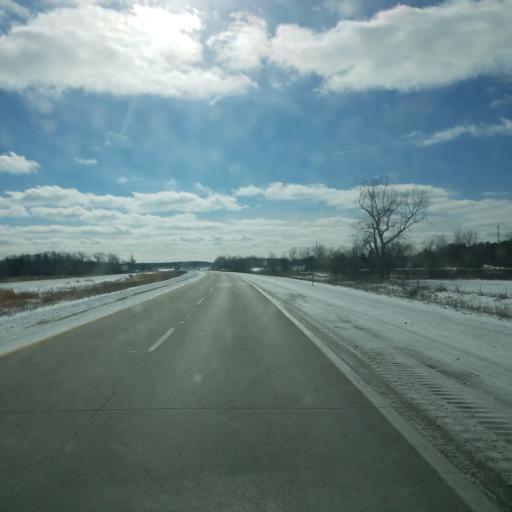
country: US
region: Michigan
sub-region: Clinton County
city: Saint Johns
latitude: 42.9192
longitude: -84.5190
